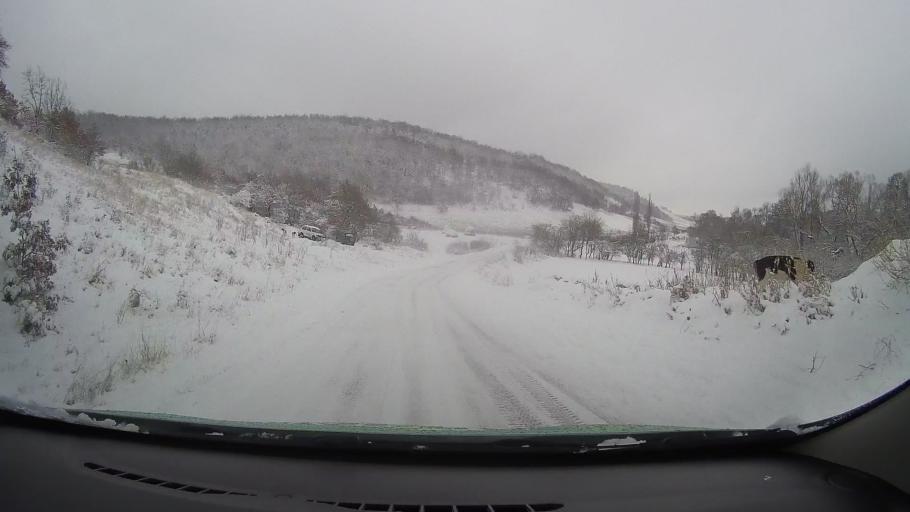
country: RO
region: Hunedoara
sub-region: Comuna Pestisu Mic
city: Pestisu Mic
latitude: 45.8232
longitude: 22.8644
